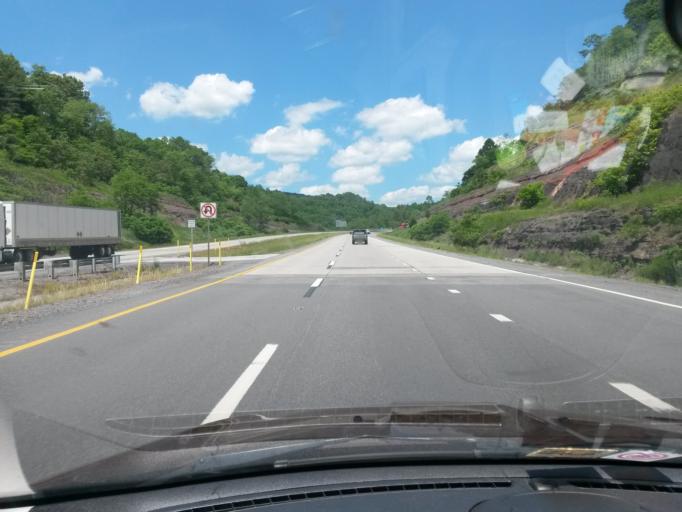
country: US
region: West Virginia
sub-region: Summers County
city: Hinton
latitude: 37.7836
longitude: -80.8898
